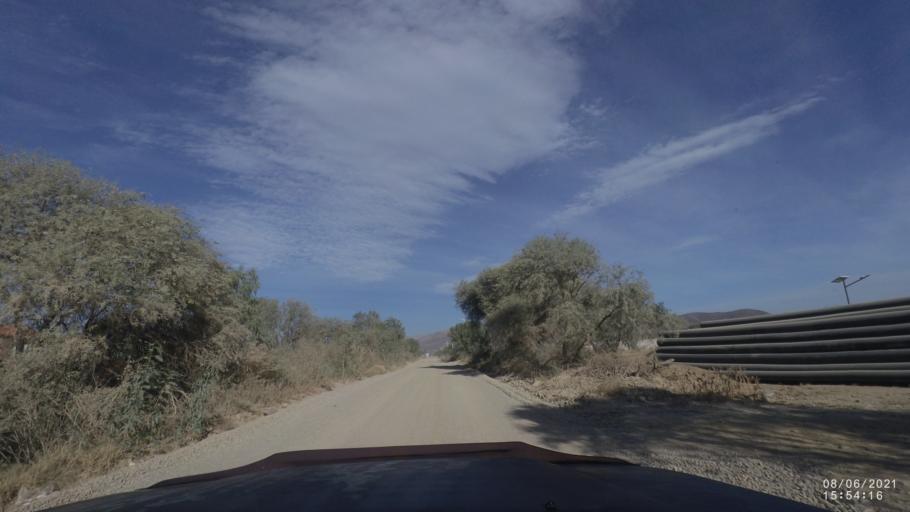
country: BO
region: Cochabamba
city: Capinota
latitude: -17.5568
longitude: -66.2542
